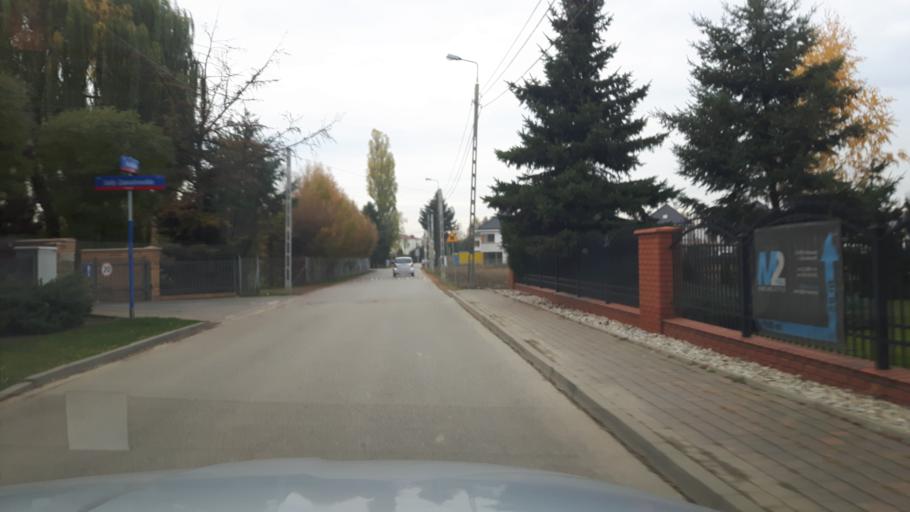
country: PL
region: Masovian Voivodeship
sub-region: Warszawa
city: Wilanow
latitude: 52.1633
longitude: 21.1221
